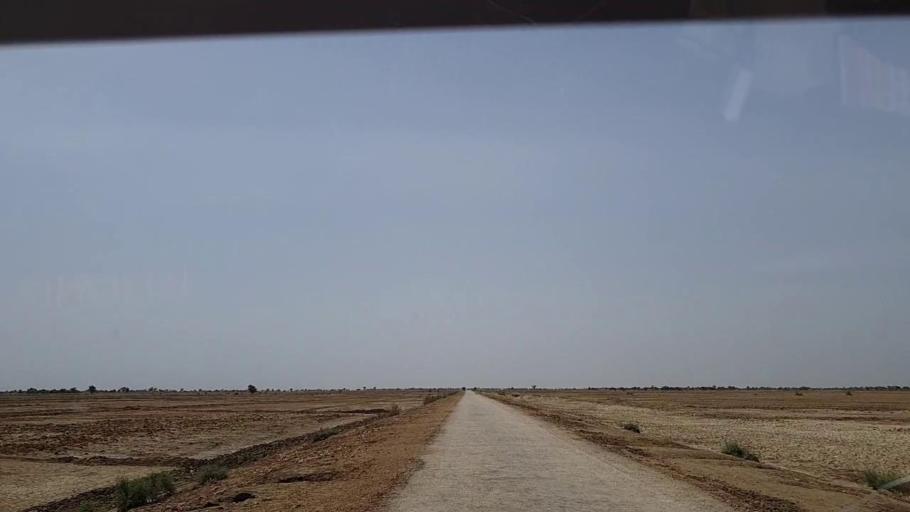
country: PK
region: Sindh
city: Johi
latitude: 26.7336
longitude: 67.6362
